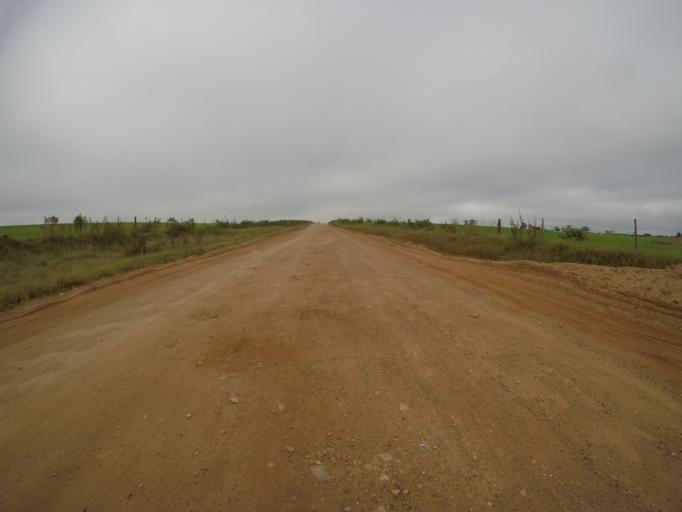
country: ZA
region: Eastern Cape
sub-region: Cacadu District Municipality
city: Kareedouw
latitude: -34.0285
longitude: 24.2431
